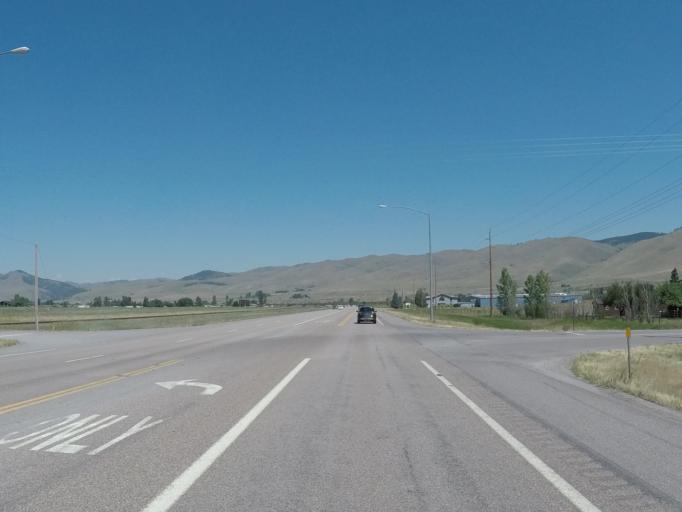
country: US
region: Montana
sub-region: Missoula County
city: Frenchtown
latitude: 47.1885
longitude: -114.1024
